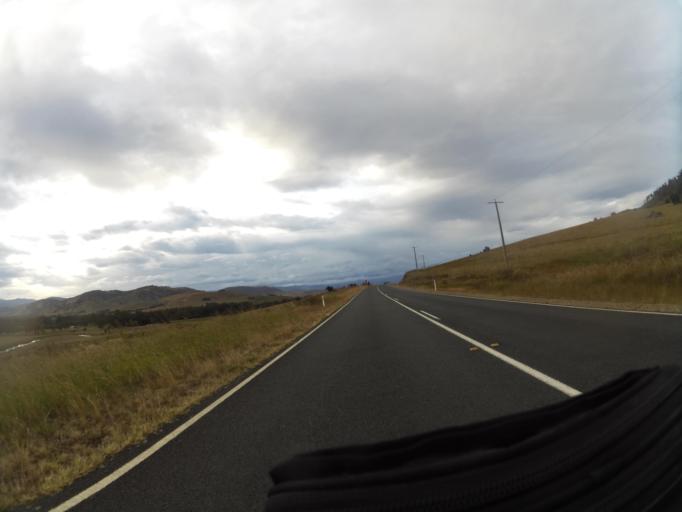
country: AU
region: New South Wales
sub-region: Snowy River
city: Jindabyne
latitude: -36.0800
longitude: 147.9748
